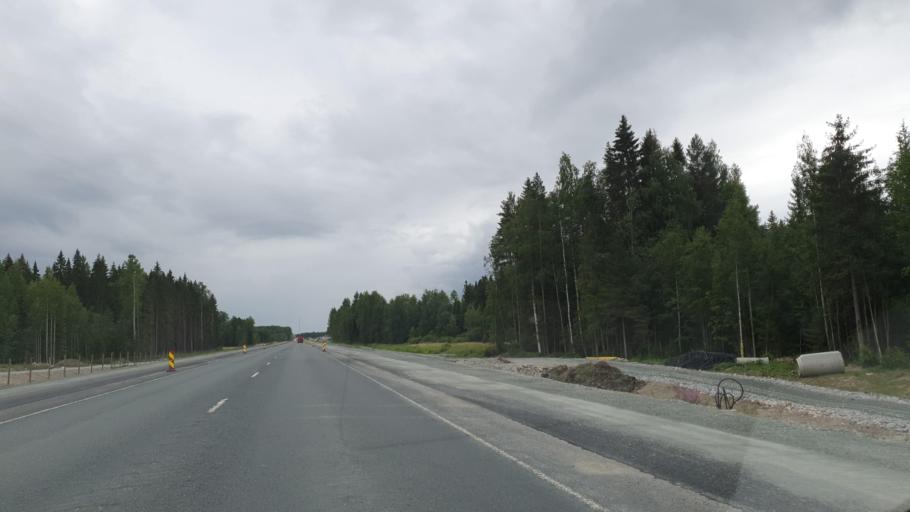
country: FI
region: Northern Savo
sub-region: Ylae-Savo
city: Lapinlahti
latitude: 63.2971
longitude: 27.4525
